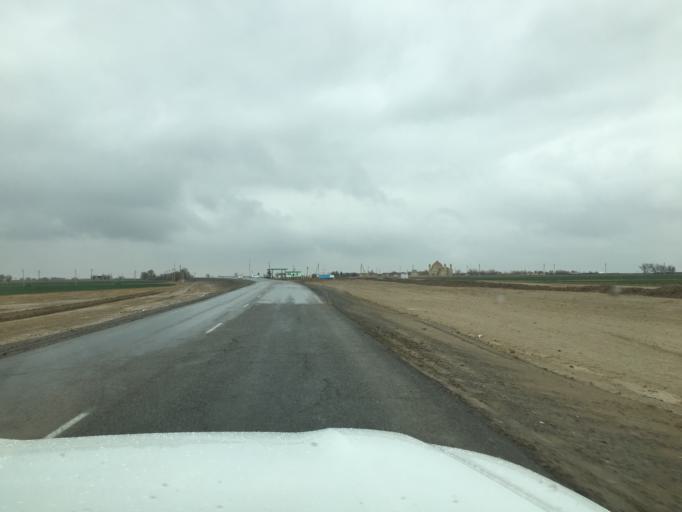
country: TM
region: Mary
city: Bayramaly
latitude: 37.4067
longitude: 62.1718
